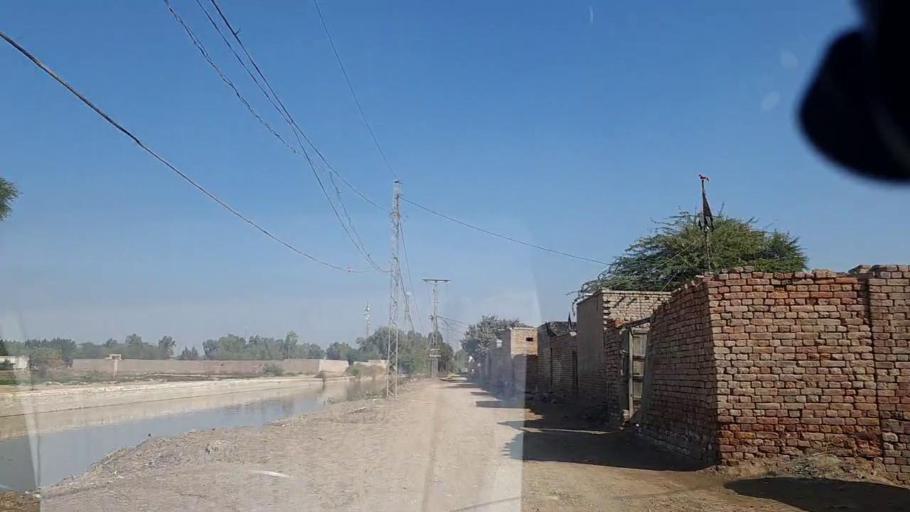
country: PK
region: Sindh
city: Khanpur
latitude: 27.8433
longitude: 69.4109
